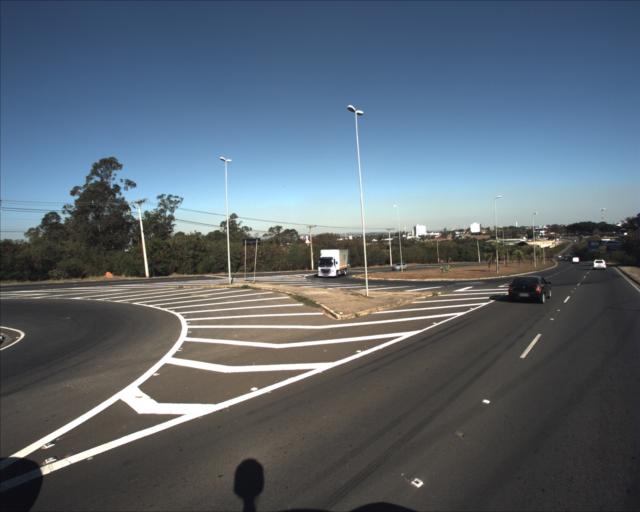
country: BR
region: Sao Paulo
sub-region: Sorocaba
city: Sorocaba
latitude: -23.4612
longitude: -47.4224
